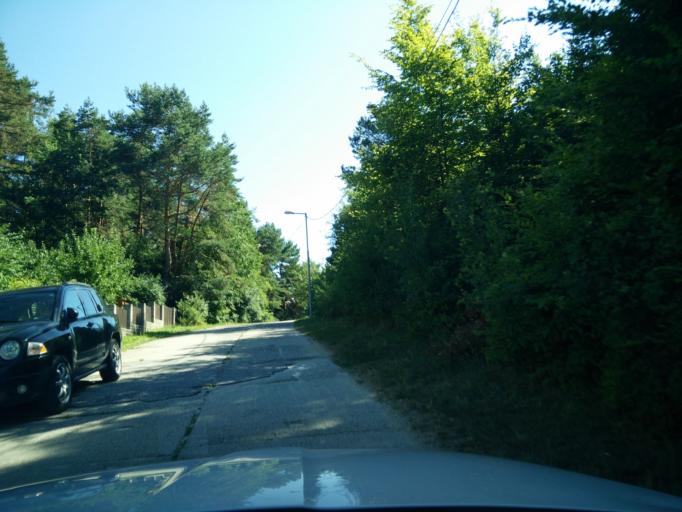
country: SK
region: Nitriansky
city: Bojnice
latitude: 48.7882
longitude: 18.5798
